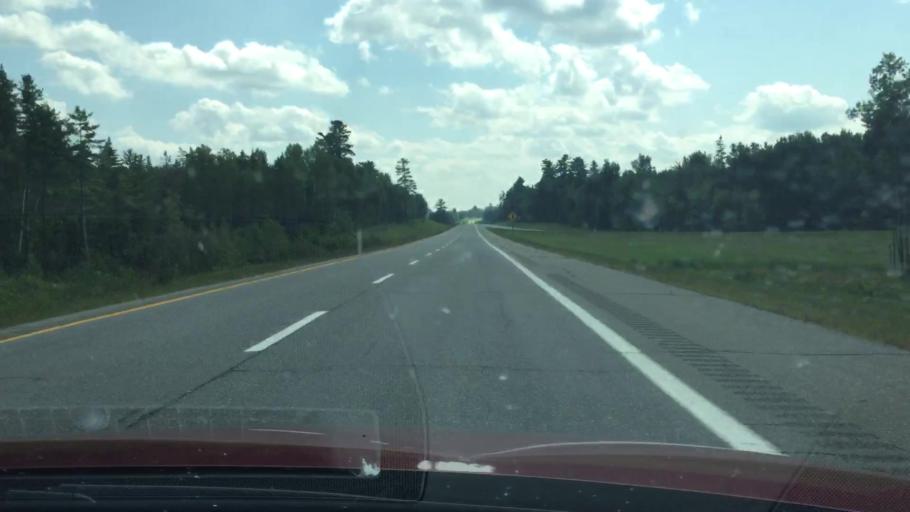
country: US
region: Maine
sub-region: Penobscot County
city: Lincoln
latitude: 45.3749
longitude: -68.6056
